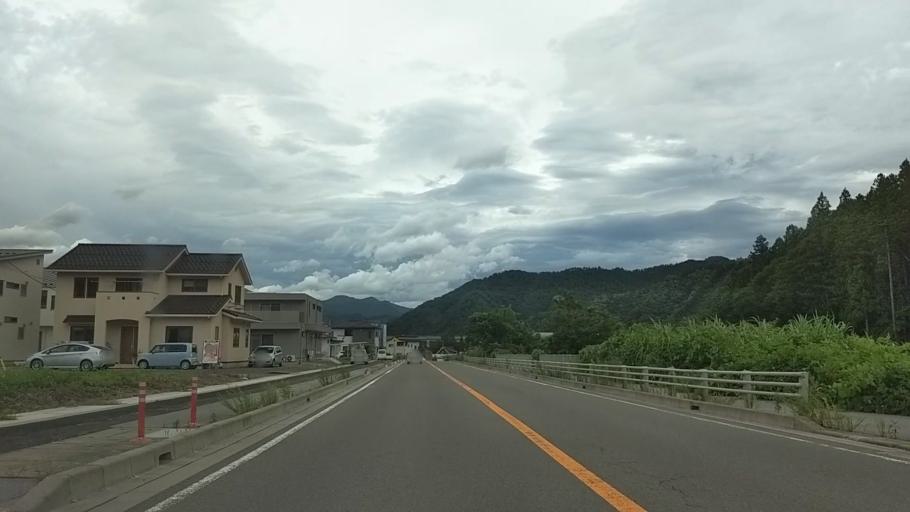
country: JP
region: Yamanashi
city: Otsuki
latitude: 35.5729
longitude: 138.9329
